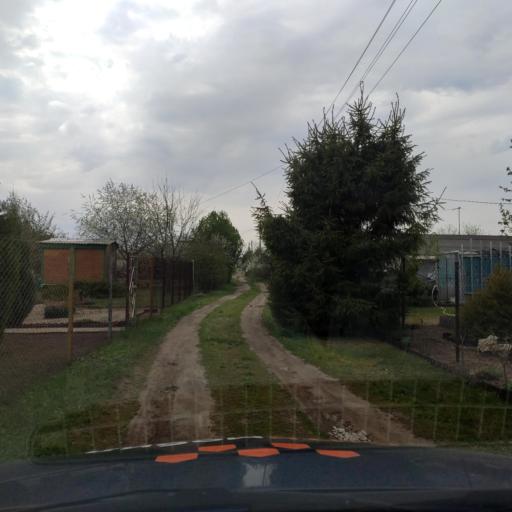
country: RU
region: Voronezj
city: Podgornoye
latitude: 51.8641
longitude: 39.1590
